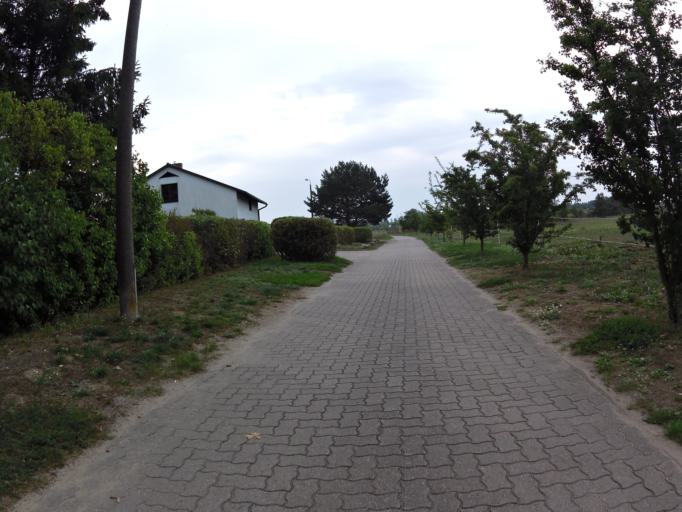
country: DE
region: Mecklenburg-Vorpommern
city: Seebad Heringsdorf
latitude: 53.8793
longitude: 14.1704
